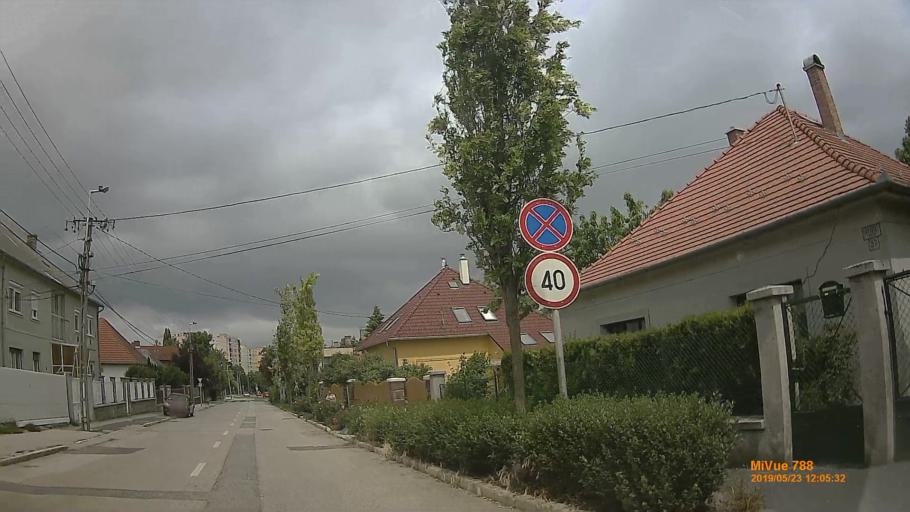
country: HU
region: Veszprem
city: Veszprem
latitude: 47.1021
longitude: 17.9212
